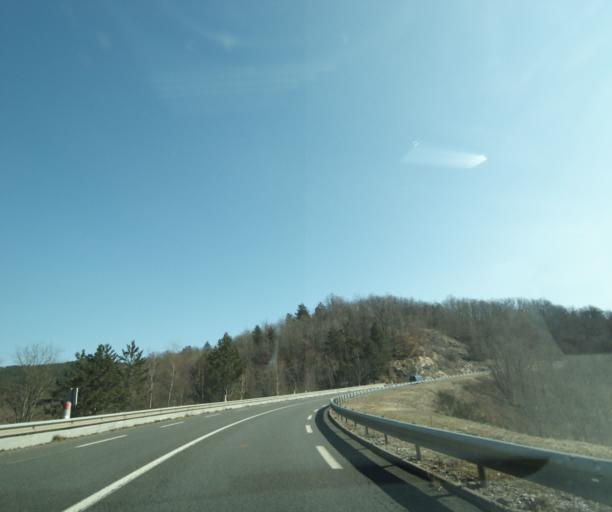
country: FR
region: Languedoc-Roussillon
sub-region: Departement de la Lozere
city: Mende
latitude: 44.5382
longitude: 3.5654
